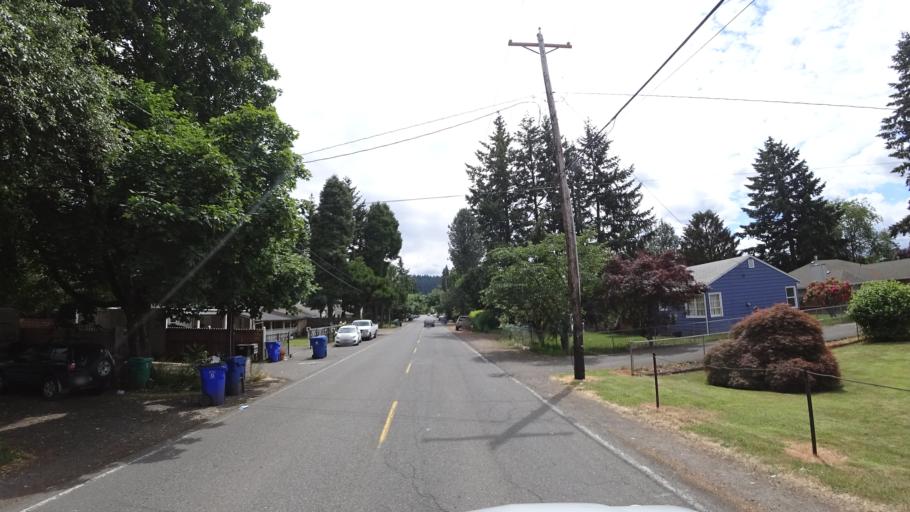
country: US
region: Oregon
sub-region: Clackamas County
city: Happy Valley
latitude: 45.5017
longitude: -122.5139
